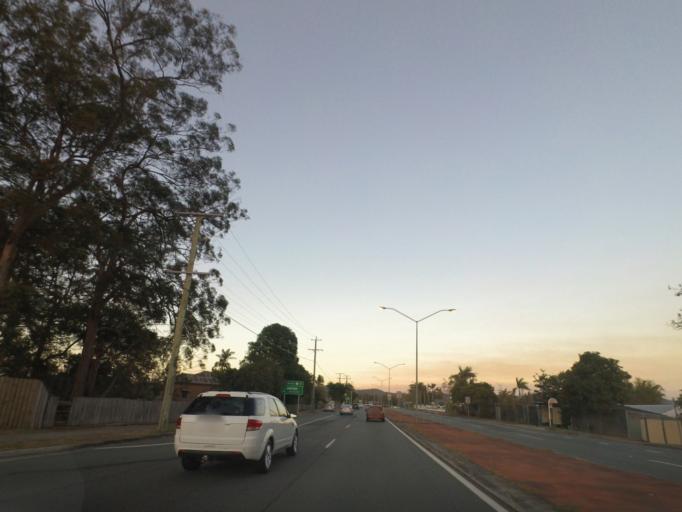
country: AU
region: Queensland
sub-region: Brisbane
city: Mackenzie
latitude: -27.5484
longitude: 153.1087
